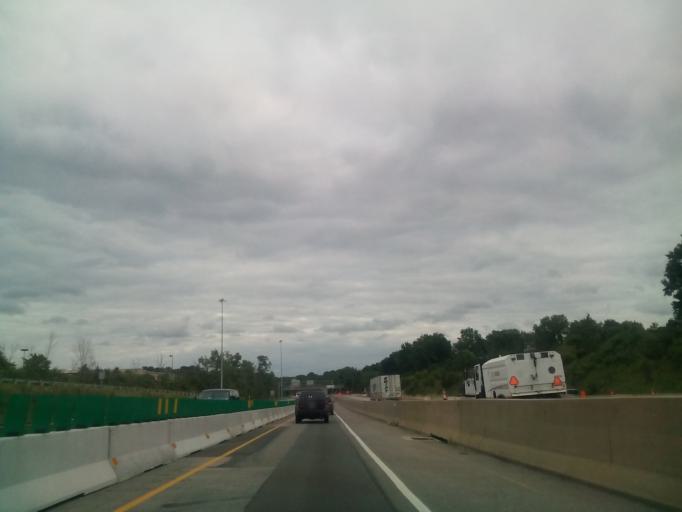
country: US
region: Ohio
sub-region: Lorain County
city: Elyria
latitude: 41.3872
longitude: -82.1106
